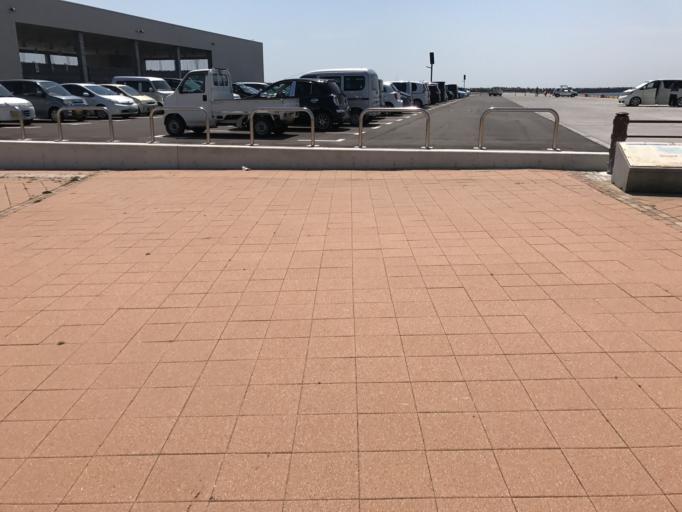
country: JP
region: Fukushima
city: Iwaki
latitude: 36.9433
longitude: 140.9060
